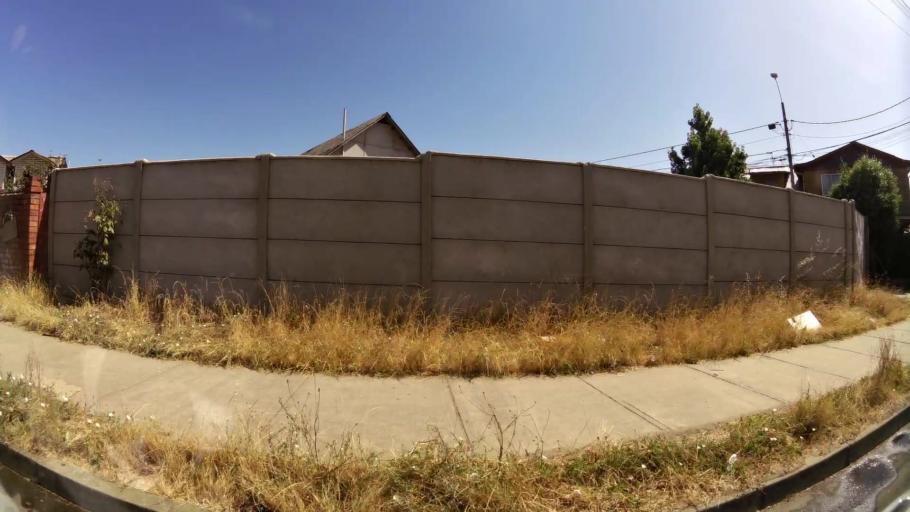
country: CL
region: Maule
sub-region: Provincia de Talca
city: Talca
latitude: -35.4135
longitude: -71.6439
